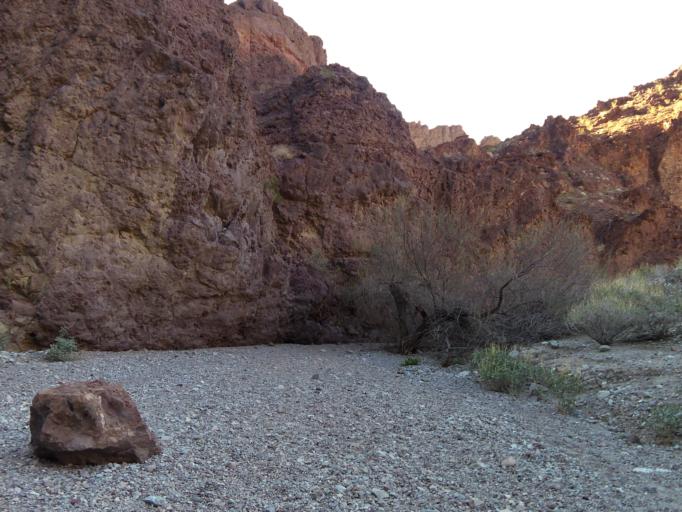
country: US
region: Nevada
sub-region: Clark County
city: Boulder City
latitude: 35.9660
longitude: -114.7251
